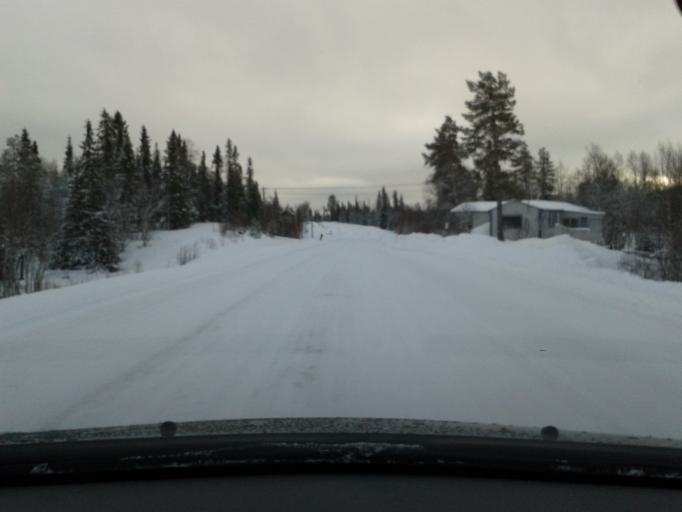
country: SE
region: Vaesterbotten
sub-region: Vilhelmina Kommun
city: Sjoberg
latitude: 65.2504
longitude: 15.7326
